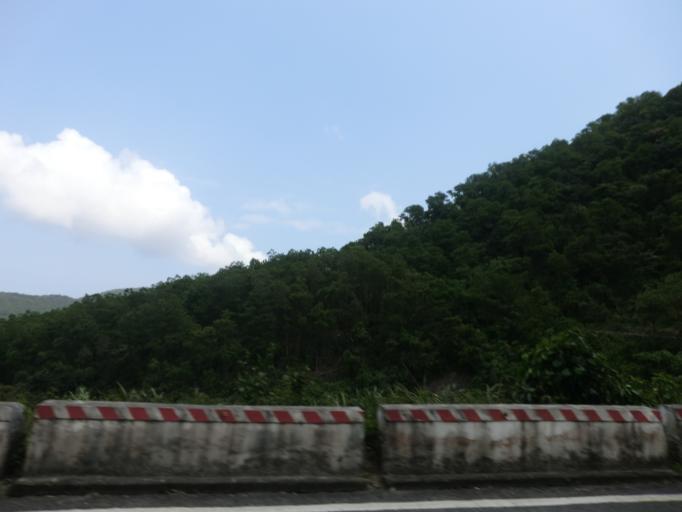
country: VN
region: Da Nang
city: Lien Chieu
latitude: 16.2009
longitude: 108.1131
